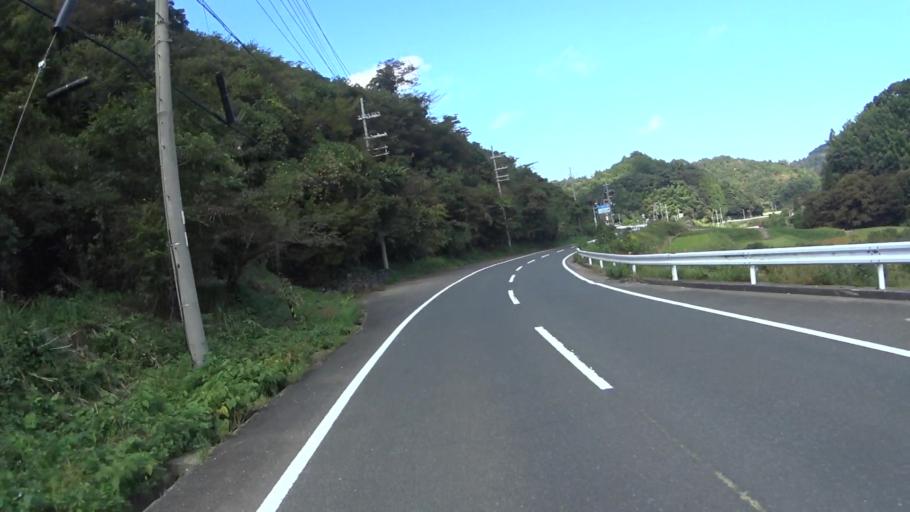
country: JP
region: Kyoto
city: Miyazu
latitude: 35.7012
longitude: 135.2500
